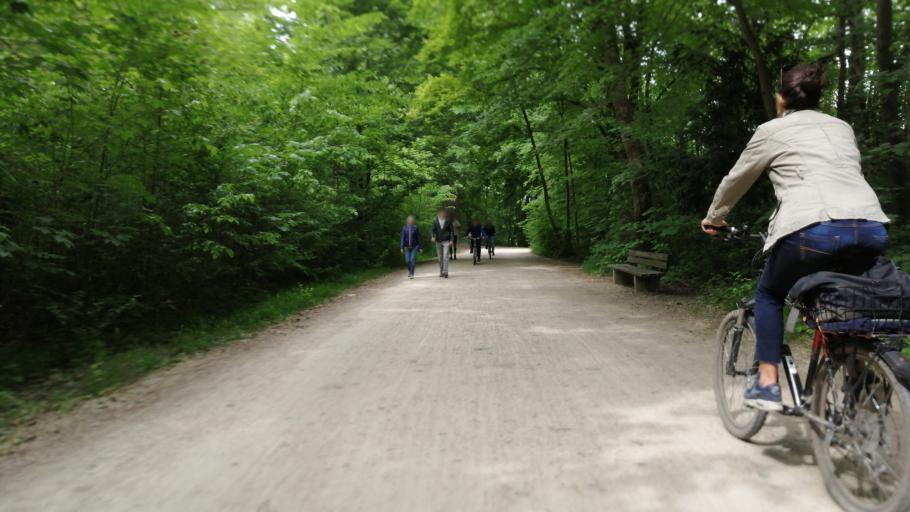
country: DE
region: Bavaria
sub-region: Upper Bavaria
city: Munich
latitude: 48.1095
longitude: 11.5586
